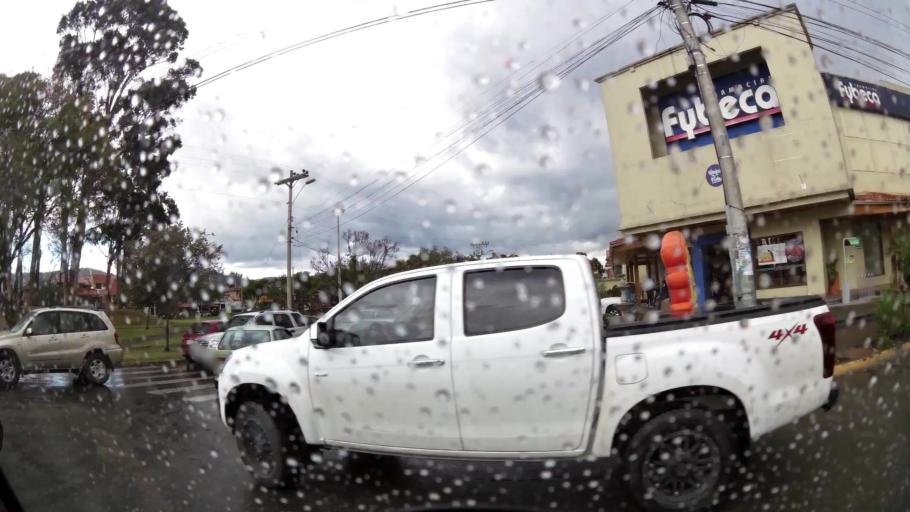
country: EC
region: Azuay
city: Cuenca
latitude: -2.8985
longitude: -79.0178
